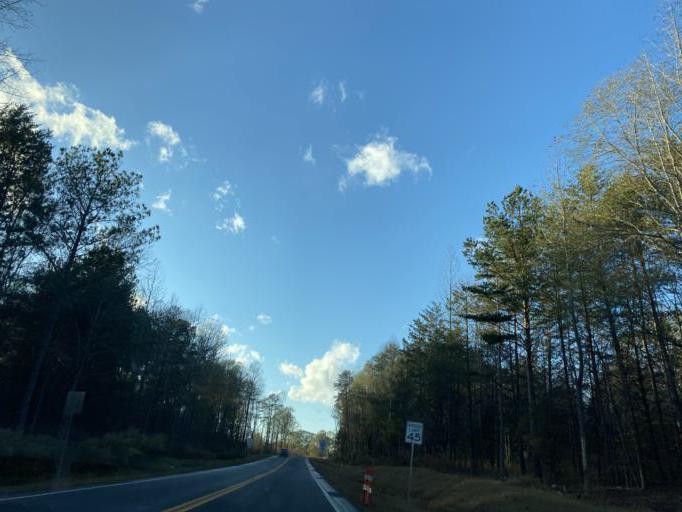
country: US
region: South Carolina
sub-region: York County
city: Clover
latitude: 35.1288
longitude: -81.2272
